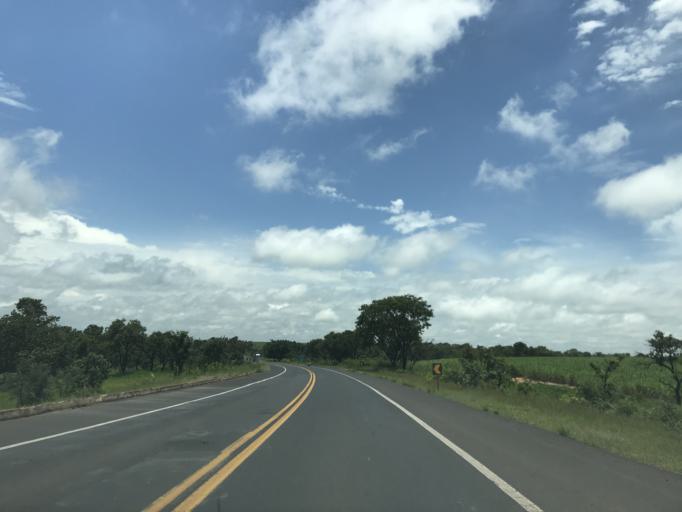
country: BR
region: Minas Gerais
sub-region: Prata
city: Prata
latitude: -19.6391
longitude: -48.8555
